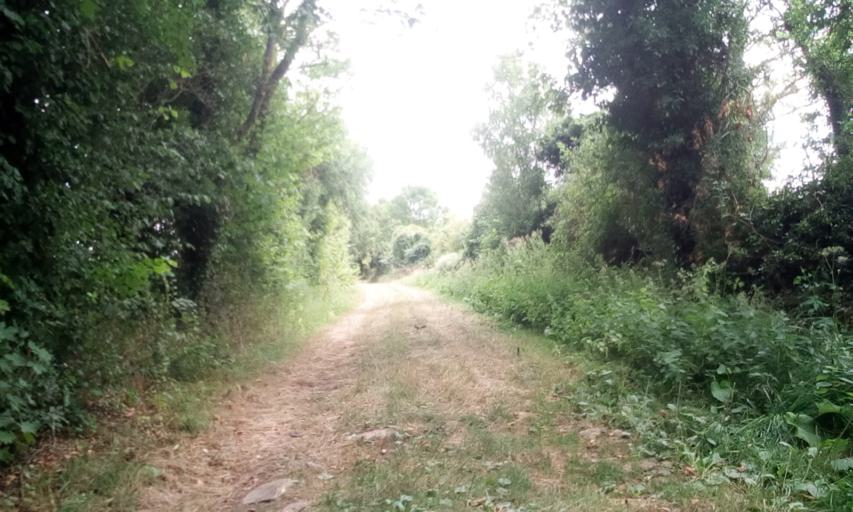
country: FR
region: Lower Normandy
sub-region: Departement du Calvados
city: Troarn
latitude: 49.1700
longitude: -0.1956
